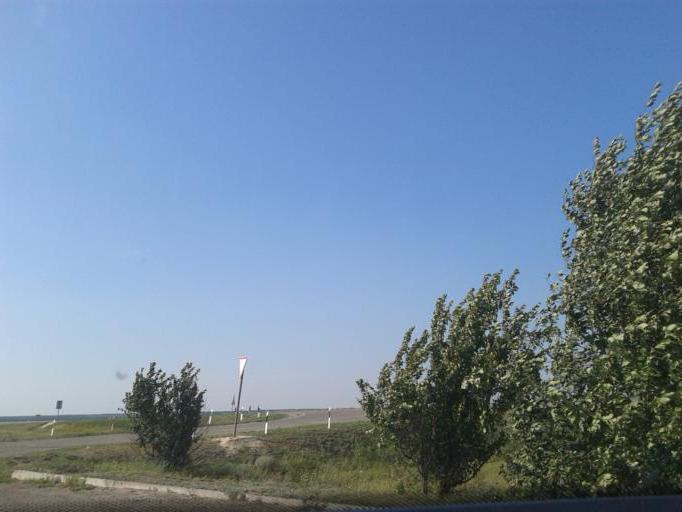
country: RU
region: Volgograd
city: Ilovlya
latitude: 49.0473
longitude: 44.1340
